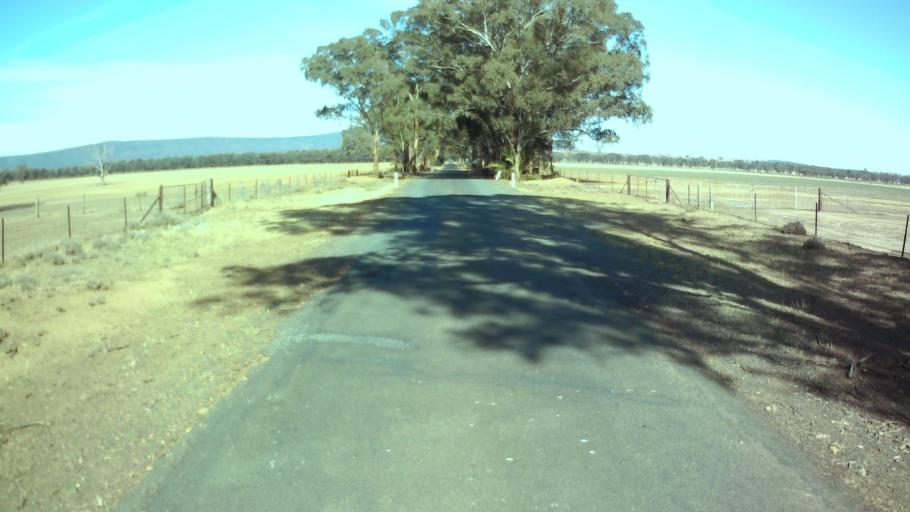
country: AU
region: New South Wales
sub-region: Weddin
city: Grenfell
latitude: -33.9067
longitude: 148.0986
